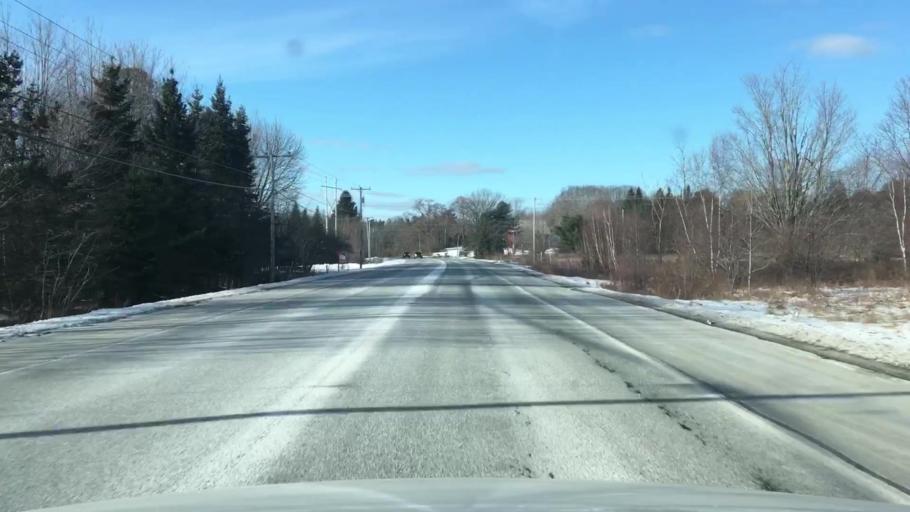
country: US
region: Maine
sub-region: Penobscot County
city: Holden
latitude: 44.8003
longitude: -68.5966
